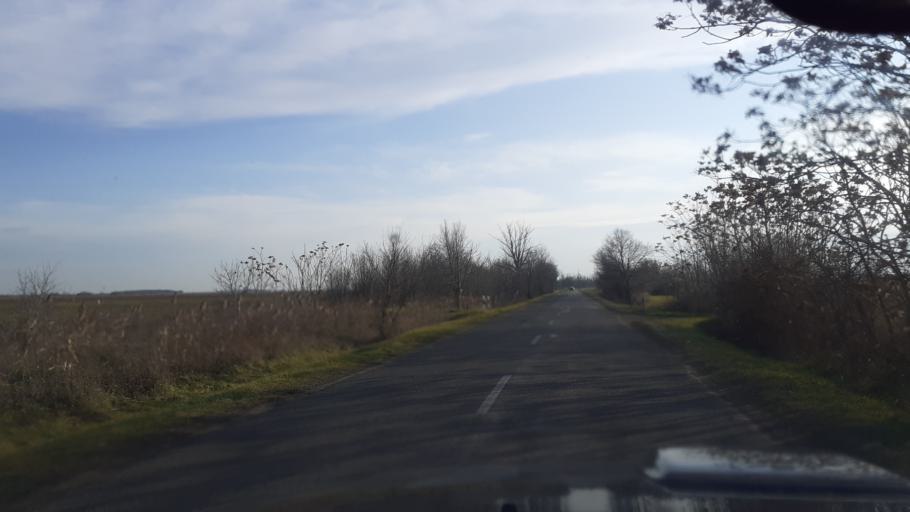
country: HU
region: Pest
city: Domsod
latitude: 47.1099
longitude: 19.0894
